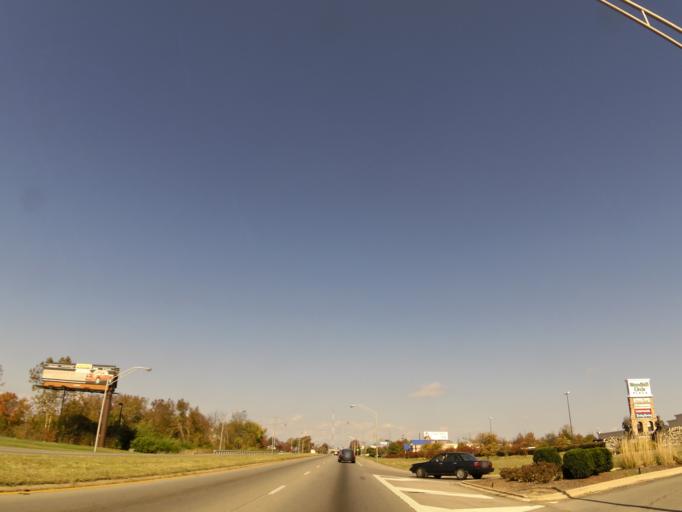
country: US
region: Kentucky
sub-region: Fayette County
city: Lexington-Fayette
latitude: 38.0196
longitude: -84.4557
